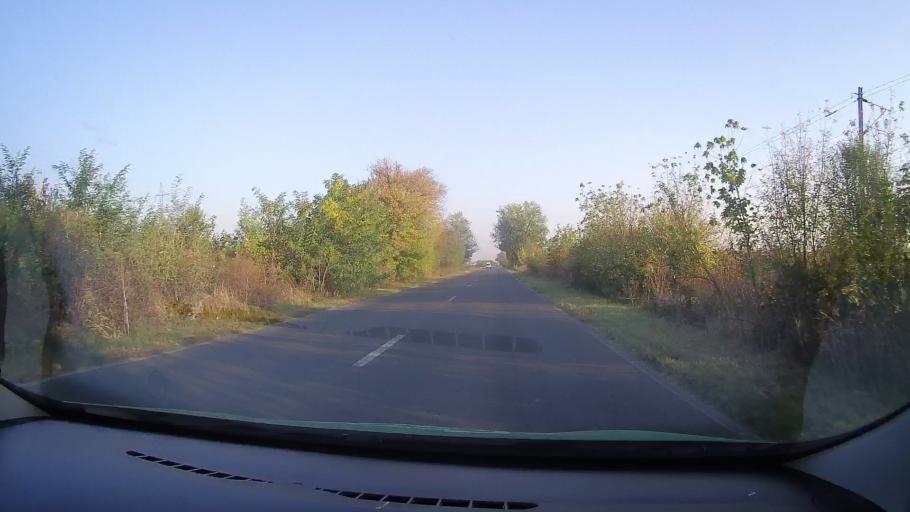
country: RO
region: Arad
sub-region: Comuna Curtici
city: Curtici
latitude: 46.3211
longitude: 21.3066
